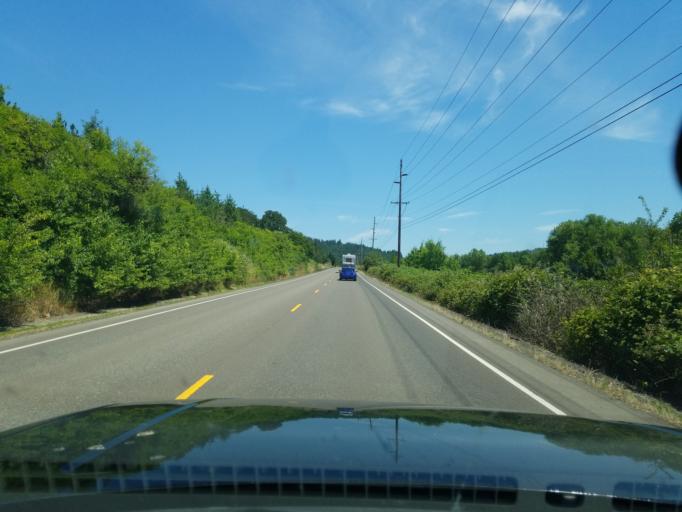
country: US
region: Oregon
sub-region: Yamhill County
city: Yamhill
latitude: 45.3660
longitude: -123.1649
